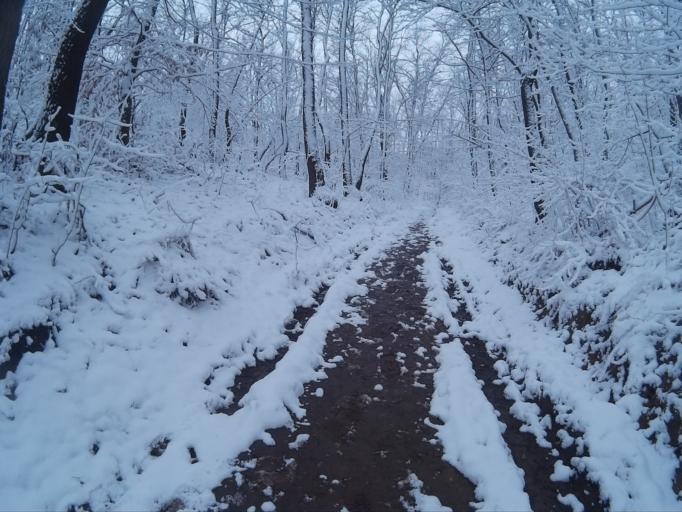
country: HU
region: Fejer
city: Szarliget
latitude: 47.5157
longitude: 18.5086
